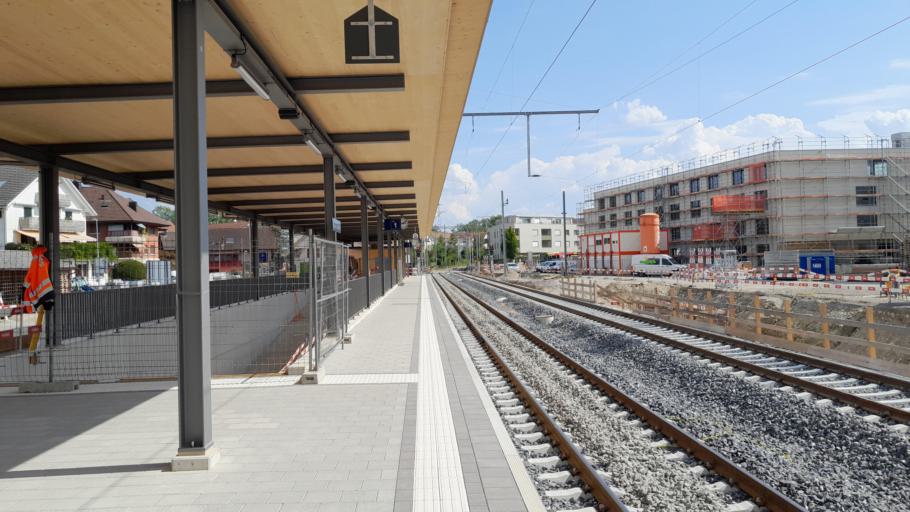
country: CH
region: Bern
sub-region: Emmental District
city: Kirchberg
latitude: 47.0833
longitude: 7.5804
